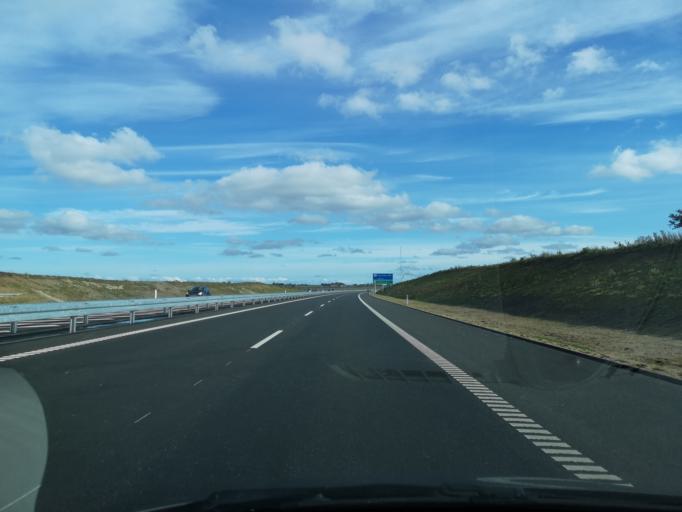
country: DK
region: Central Jutland
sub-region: Holstebro Kommune
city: Holstebro
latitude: 56.3889
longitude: 8.6281
